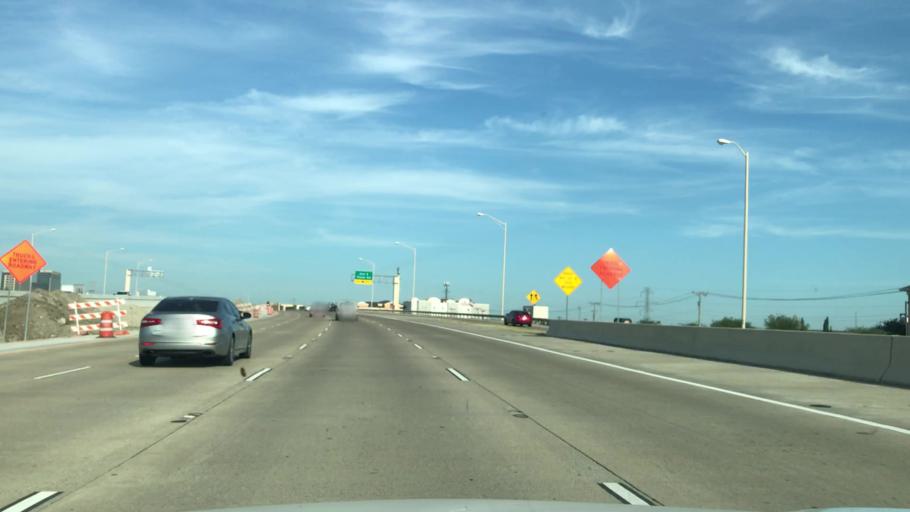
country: US
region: Texas
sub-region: Collin County
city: Plano
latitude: 33.0022
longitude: -96.6787
